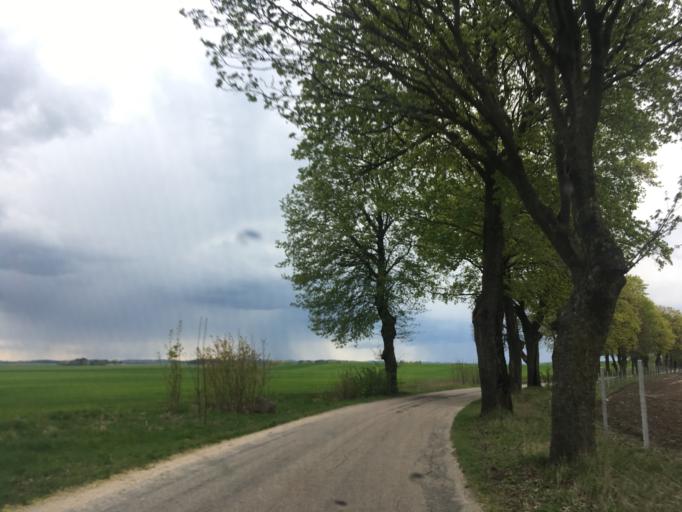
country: PL
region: Warmian-Masurian Voivodeship
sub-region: Powiat ostrodzki
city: Dabrowno
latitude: 53.4132
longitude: 20.1383
